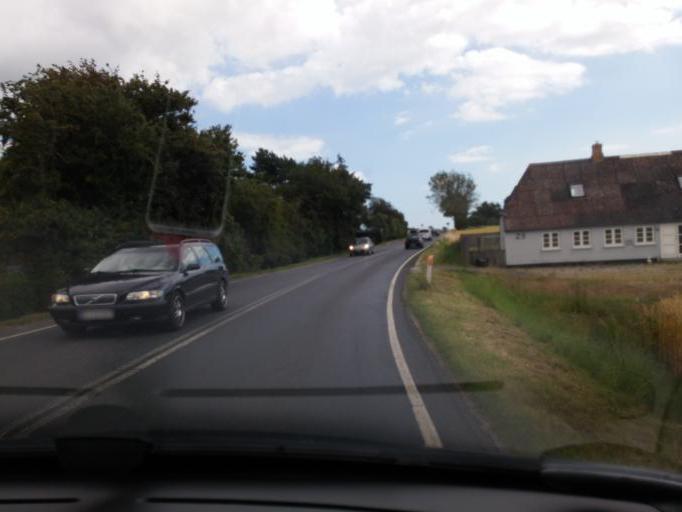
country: DK
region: South Denmark
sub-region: Langeland Kommune
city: Rudkobing
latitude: 54.9057
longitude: 10.7348
